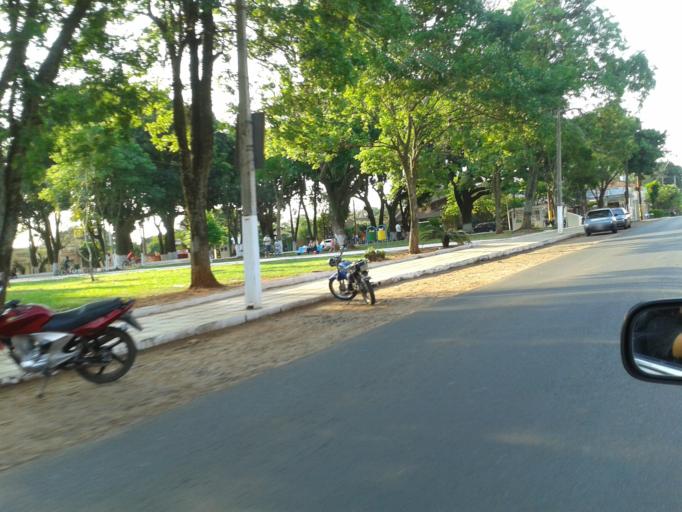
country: PY
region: Guaira
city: Villarrica
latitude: -25.7714
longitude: -56.4462
